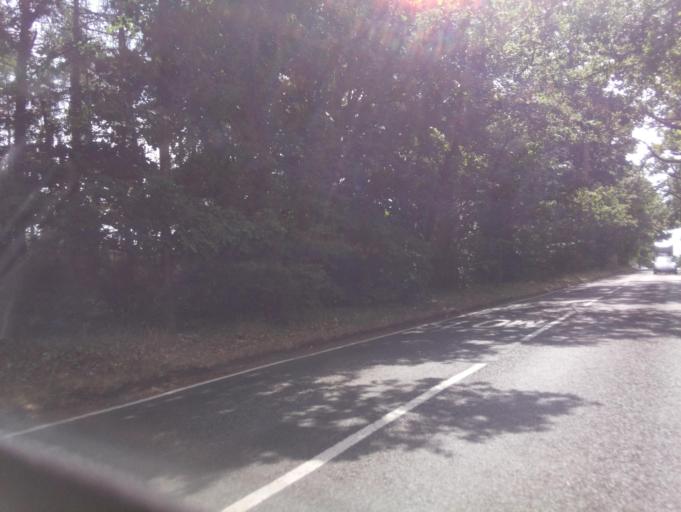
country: GB
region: England
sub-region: Surrey
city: Pirbright
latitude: 51.3008
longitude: -0.6459
